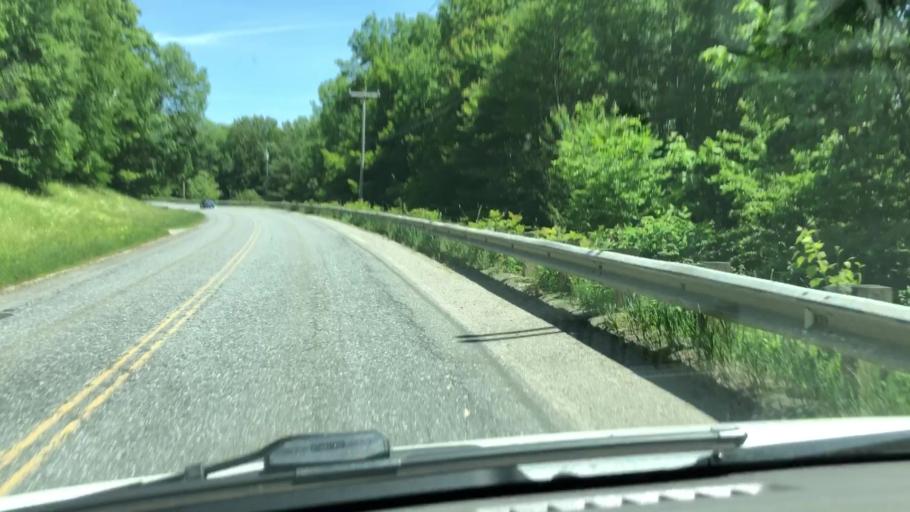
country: US
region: Massachusetts
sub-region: Franklin County
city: Charlemont
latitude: 42.5159
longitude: -72.9206
